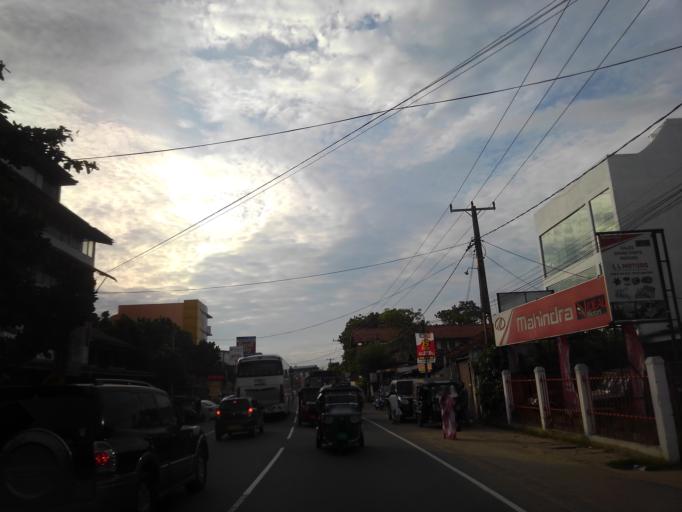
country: LK
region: Southern
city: Unawatuna
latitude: 6.0335
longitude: 80.2379
